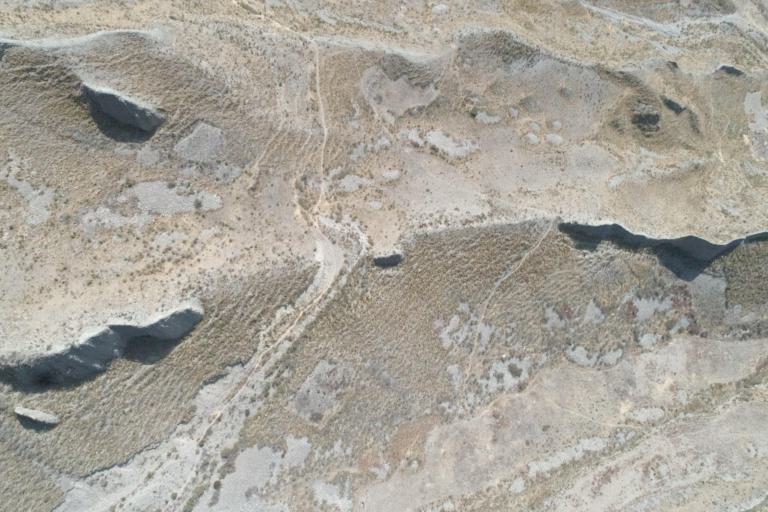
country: BO
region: La Paz
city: La Paz
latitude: -16.4744
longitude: -68.0961
